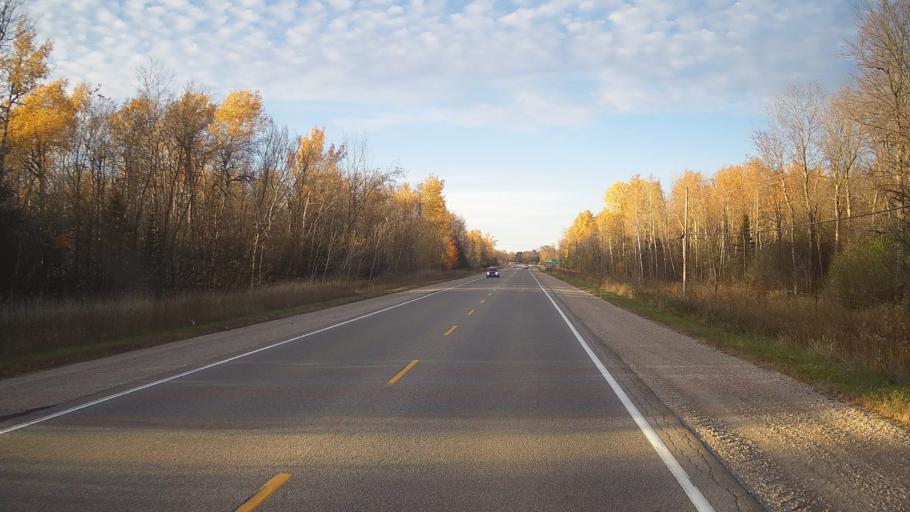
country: CA
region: Ontario
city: Perth
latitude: 45.0072
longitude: -76.2300
